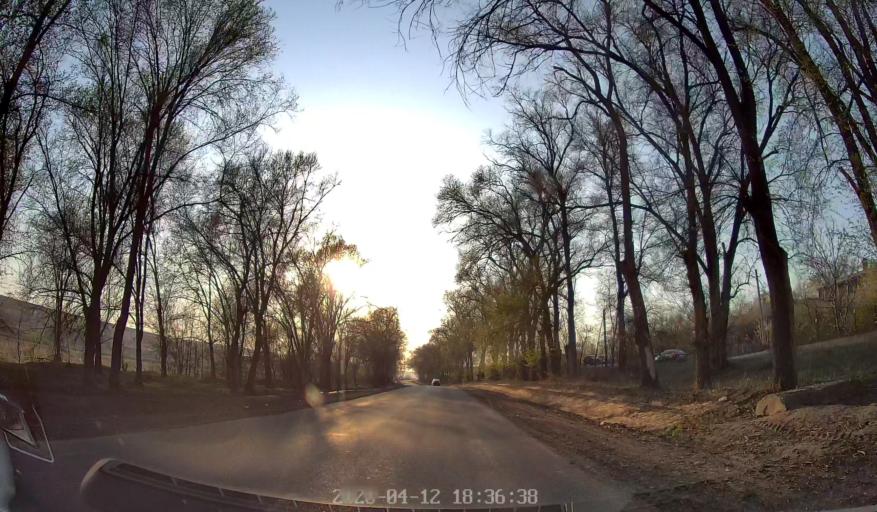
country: MD
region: Chisinau
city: Vadul lui Voda
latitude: 47.1173
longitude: 29.0271
